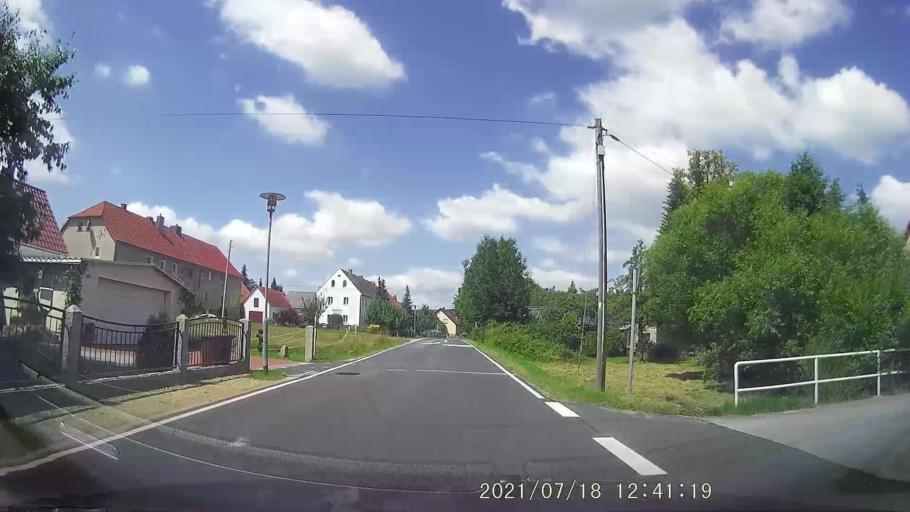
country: DE
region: Saxony
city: Konigshain
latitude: 51.1834
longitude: 14.8541
